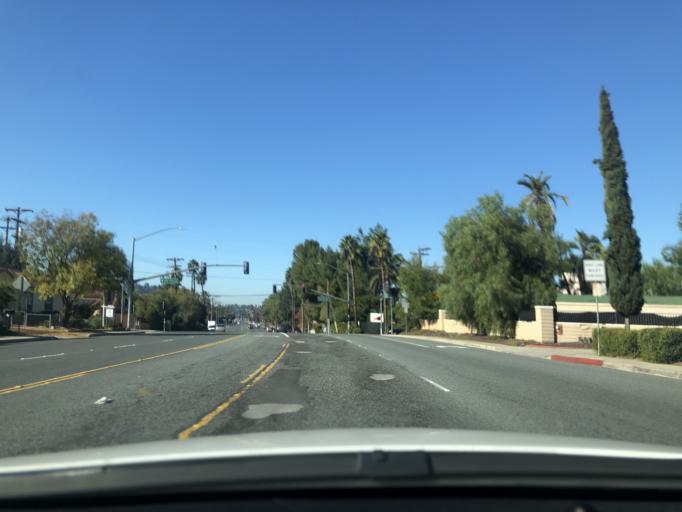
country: US
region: California
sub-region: San Diego County
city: El Cajon
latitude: 32.7804
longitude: -116.9475
